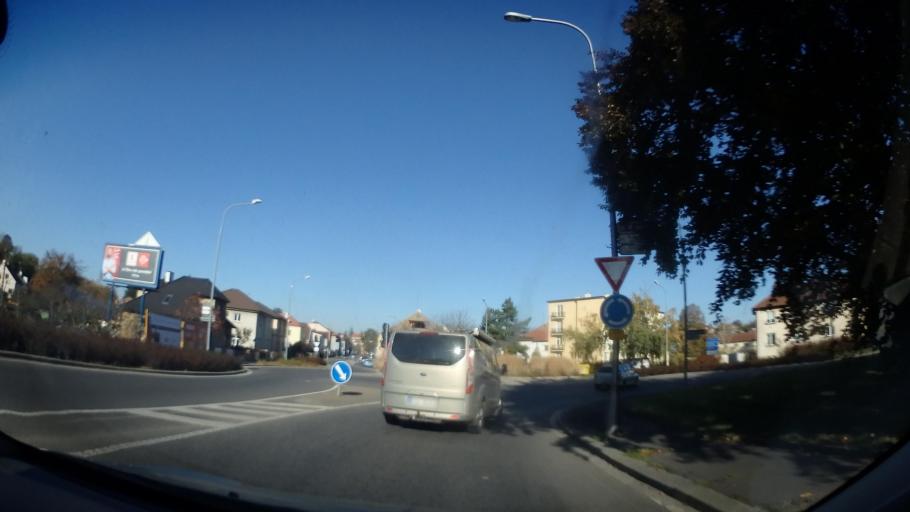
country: CZ
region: Pardubicky
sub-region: Okres Chrudim
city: Chrudim
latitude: 49.9407
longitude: 15.7946
